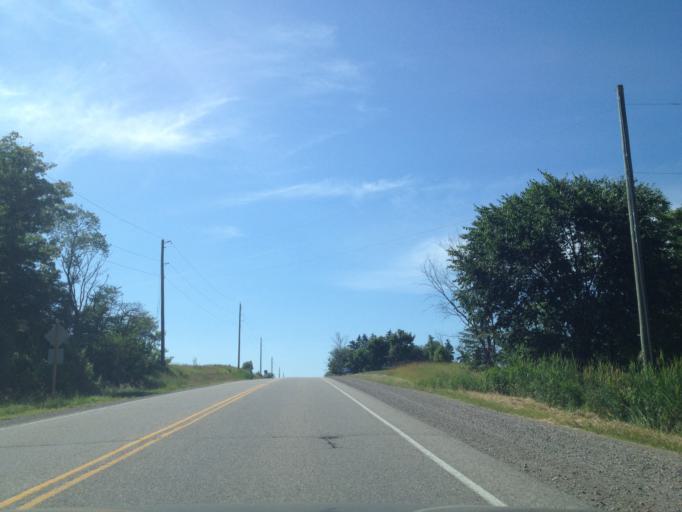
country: CA
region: Ontario
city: Stratford
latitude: 43.4691
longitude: -80.7981
